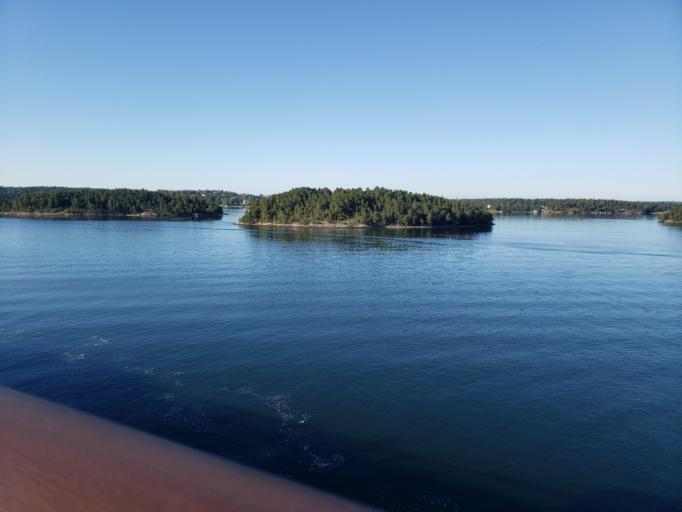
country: SE
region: Stockholm
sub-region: Vaxholms Kommun
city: Vaxholm
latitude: 59.4308
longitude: 18.3840
